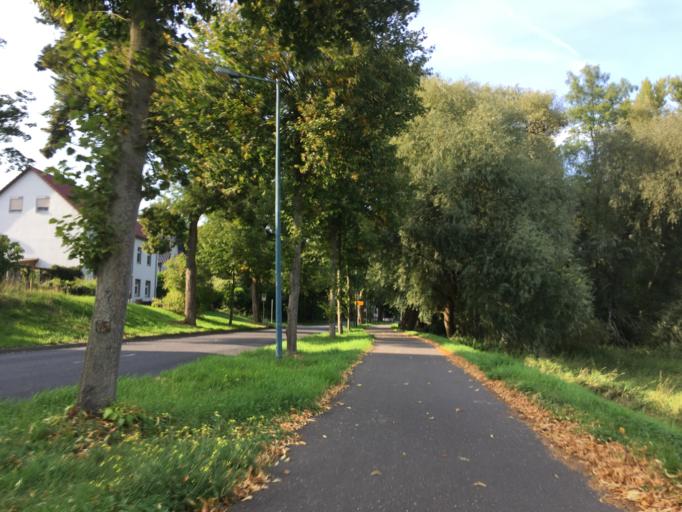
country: DE
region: Brandenburg
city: Frankfurt (Oder)
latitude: 52.3125
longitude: 14.5560
